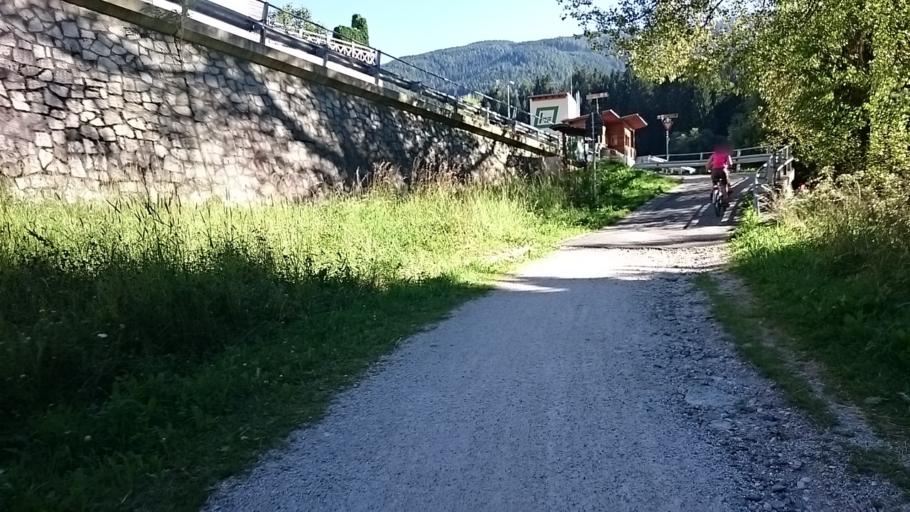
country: IT
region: Trentino-Alto Adige
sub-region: Bolzano
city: Monguelfo
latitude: 46.7595
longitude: 12.0996
